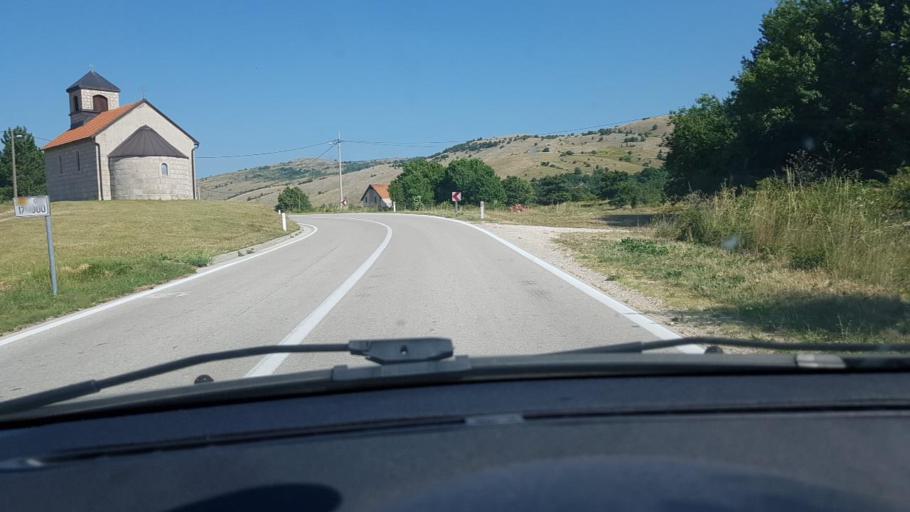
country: BA
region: Federation of Bosnia and Herzegovina
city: Bosansko Grahovo
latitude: 44.1184
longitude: 16.5366
